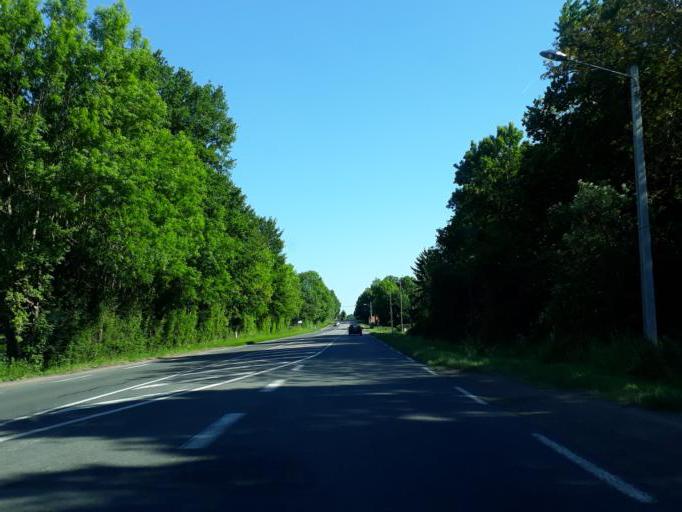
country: FR
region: Centre
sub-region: Departement du Cher
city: Lere
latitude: 47.4811
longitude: 2.9250
